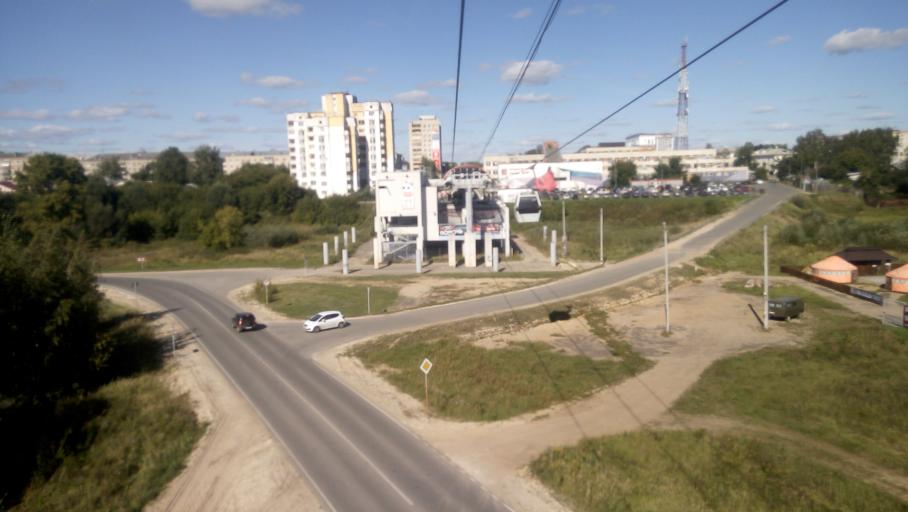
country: RU
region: Nizjnij Novgorod
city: Bor
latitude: 56.3533
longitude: 44.0604
